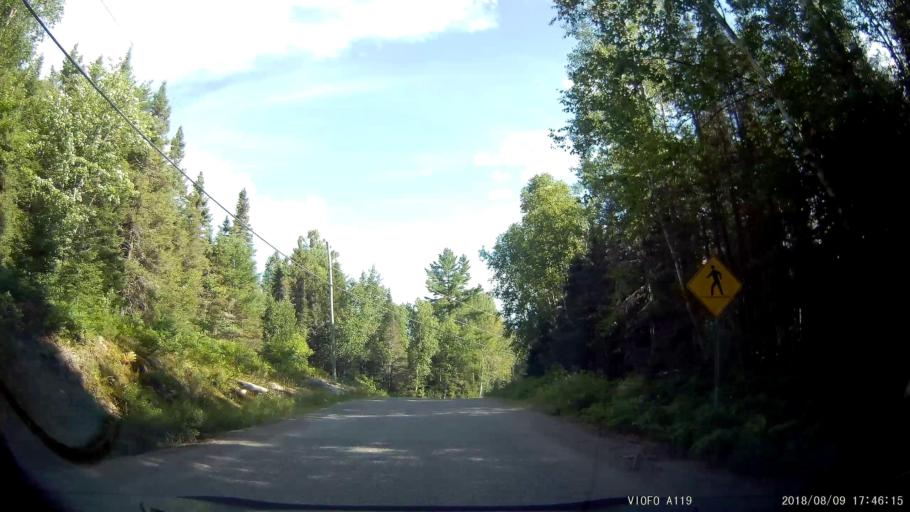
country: CA
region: Ontario
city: Rayside-Balfour
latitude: 46.5957
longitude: -81.5322
